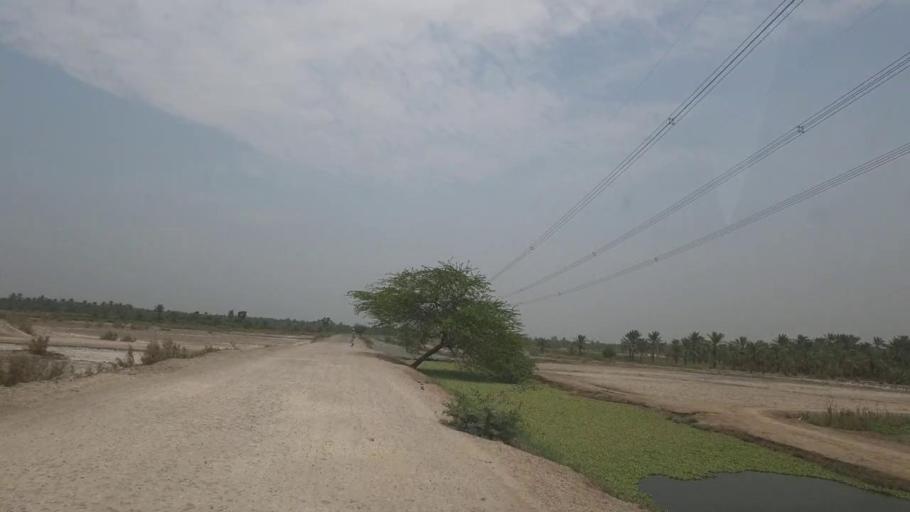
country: PK
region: Sindh
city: Kot Diji
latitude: 27.4249
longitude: 68.6874
